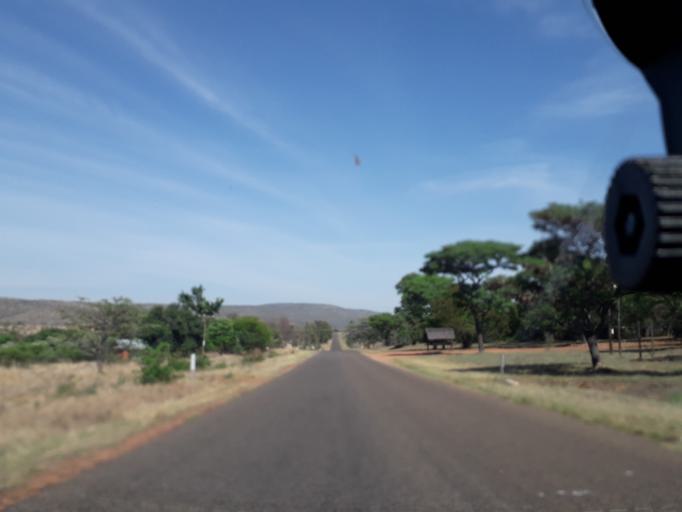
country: ZA
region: Limpopo
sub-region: Waterberg District Municipality
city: Warmbaths
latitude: -24.8409
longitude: 28.2459
